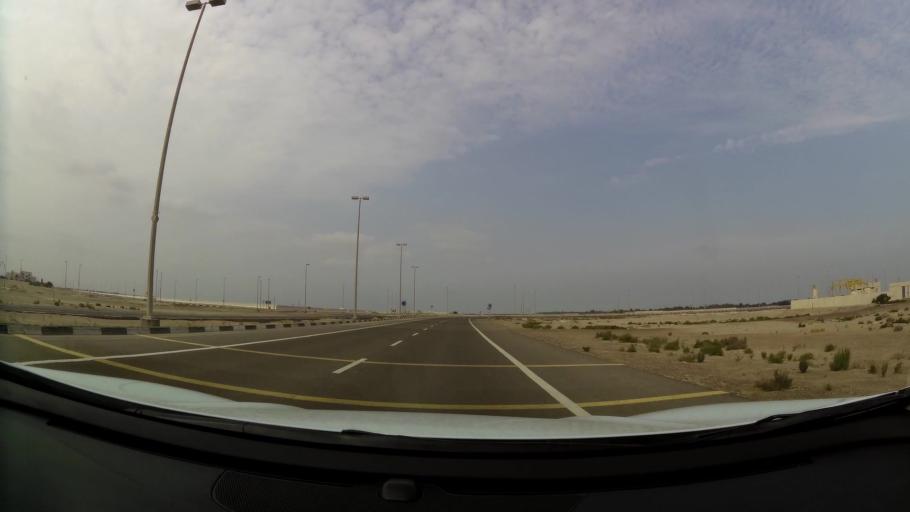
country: AE
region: Abu Dhabi
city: Abu Dhabi
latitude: 24.6392
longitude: 54.6657
